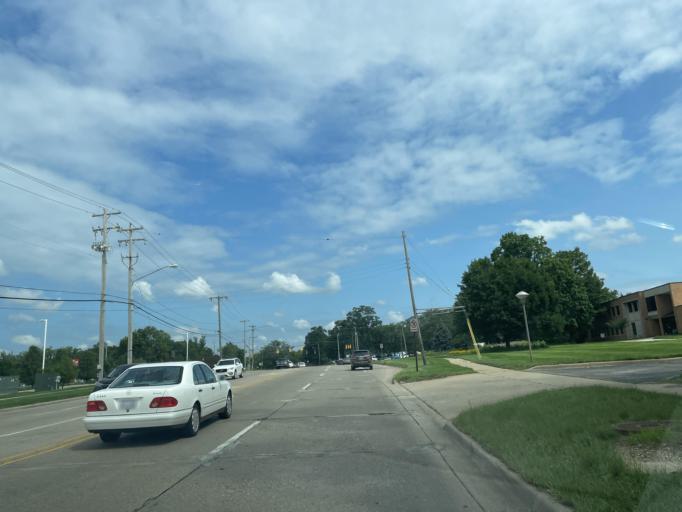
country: US
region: Michigan
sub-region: Kent County
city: East Grand Rapids
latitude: 42.9110
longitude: -85.6275
